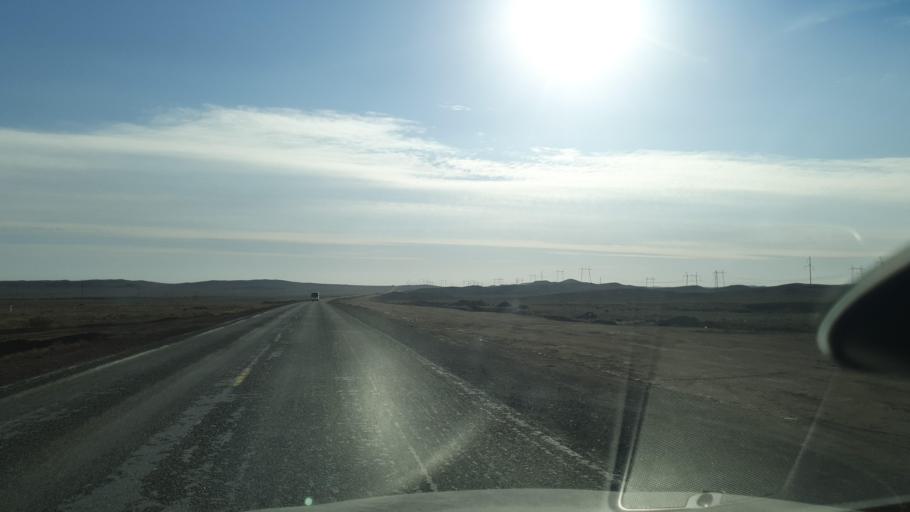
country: KZ
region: Zhambyl
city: Mynaral
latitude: 45.6874
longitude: 73.4005
